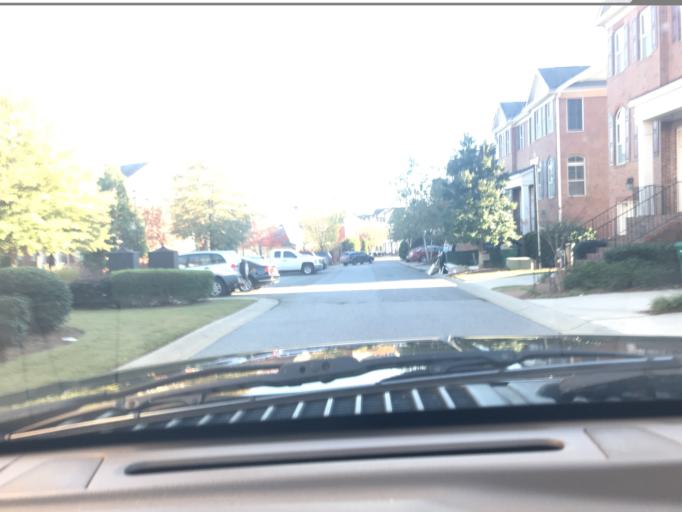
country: US
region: Georgia
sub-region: Fulton County
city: Johns Creek
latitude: 34.0451
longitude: -84.2201
